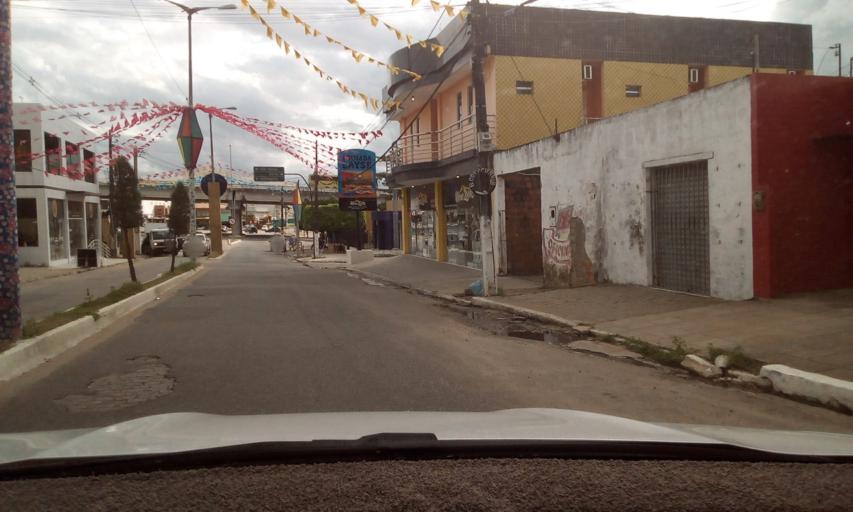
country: BR
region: Paraiba
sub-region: Mamanguape
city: Mamanguape
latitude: -6.8385
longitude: -35.1352
